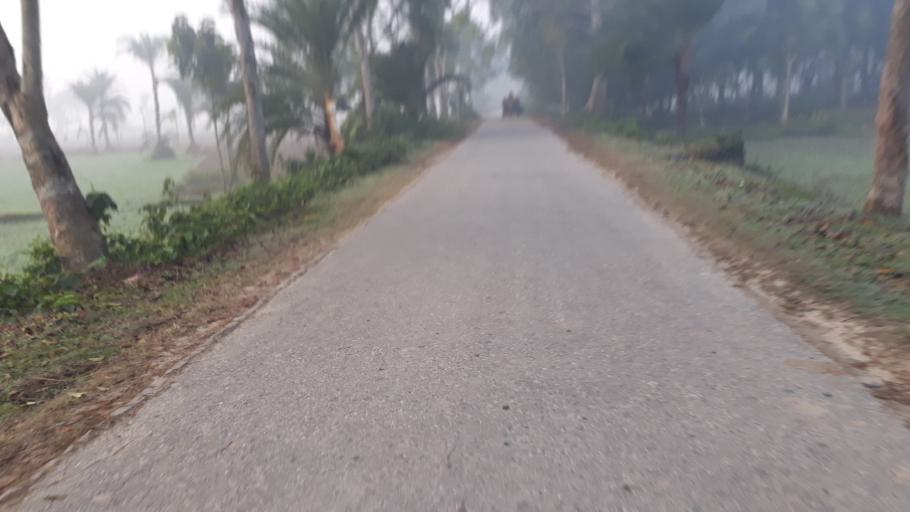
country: BD
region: Khulna
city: Jhingergacha
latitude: 23.2645
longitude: 88.9350
